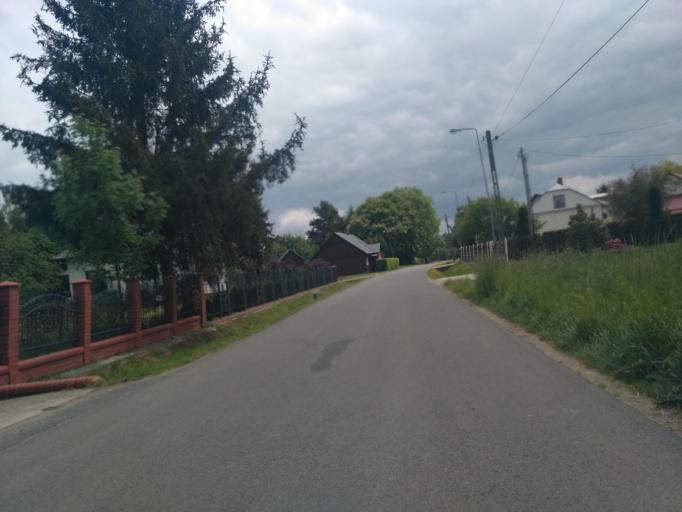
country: PL
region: Subcarpathian Voivodeship
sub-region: Powiat krosnienski
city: Jedlicze
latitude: 49.7063
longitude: 21.6367
